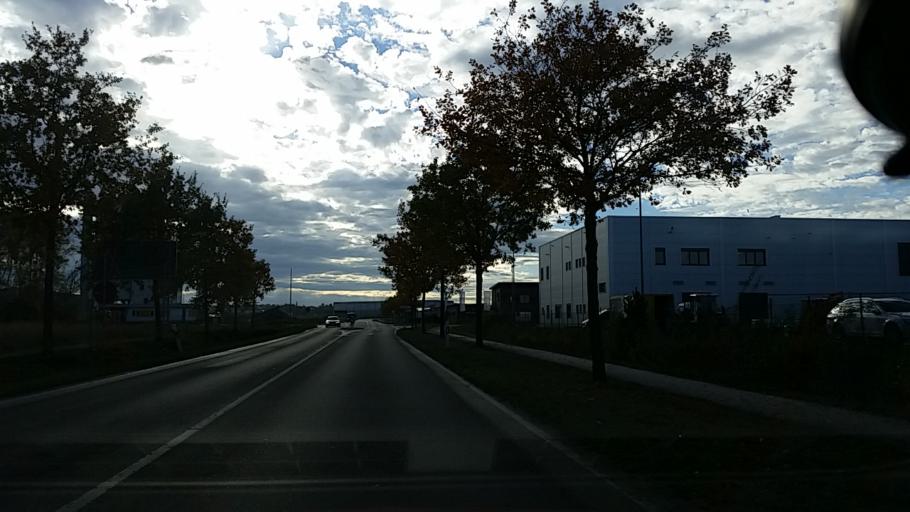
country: DE
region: Lower Saxony
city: Danndorf
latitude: 52.4281
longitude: 10.8733
